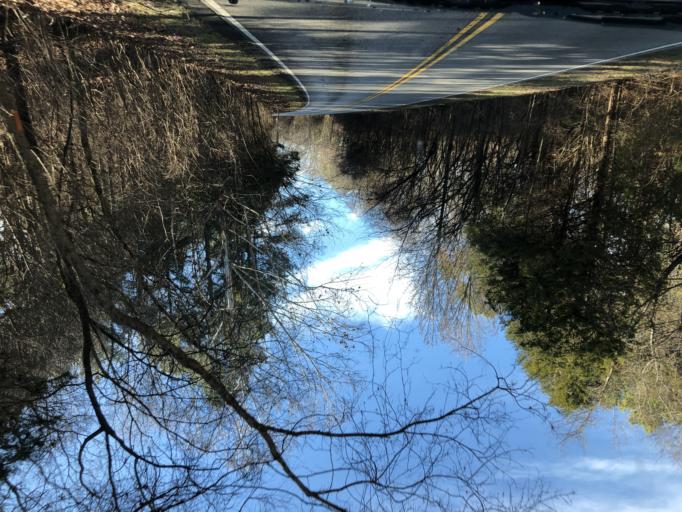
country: US
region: Tennessee
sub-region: Davidson County
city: Lakewood
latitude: 36.1656
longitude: -86.6102
